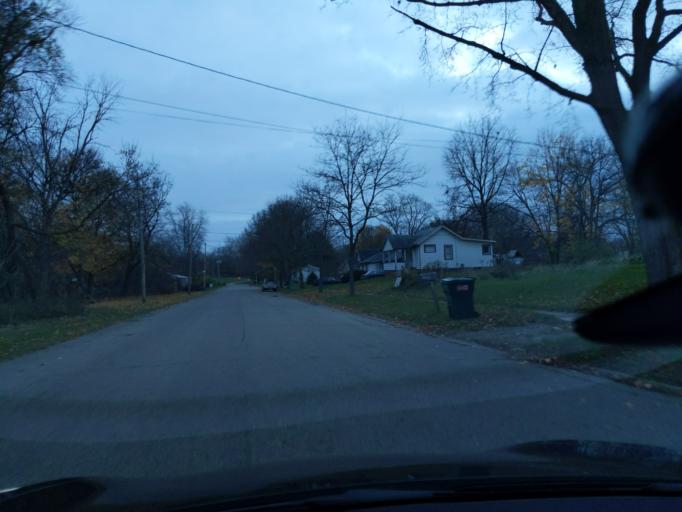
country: US
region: Michigan
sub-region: Ingham County
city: East Lansing
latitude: 42.7278
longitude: -84.5152
